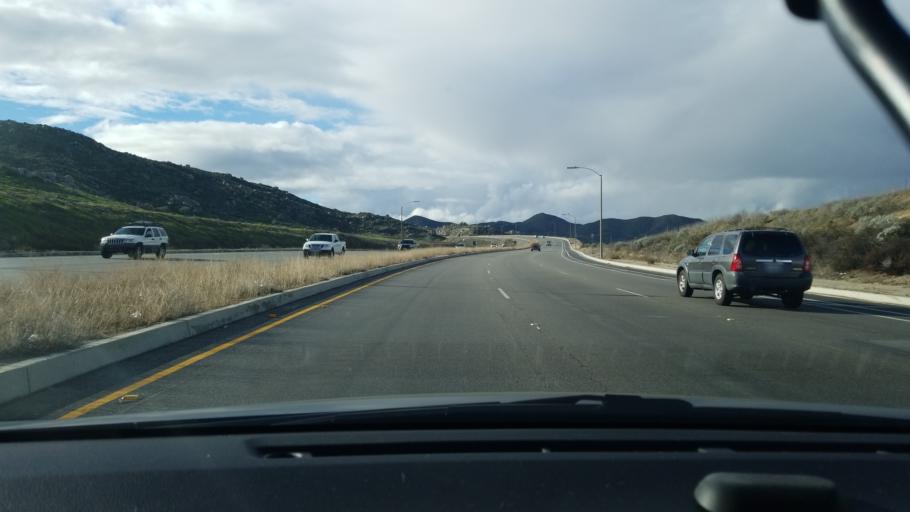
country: US
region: California
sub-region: Riverside County
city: Menifee
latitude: 33.6928
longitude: -117.1286
